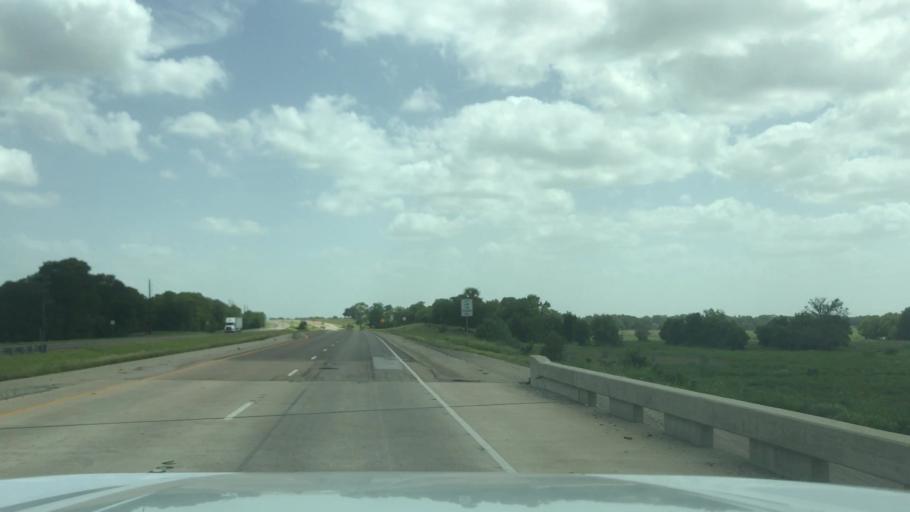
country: US
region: Texas
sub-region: Robertson County
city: Calvert
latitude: 31.0145
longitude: -96.7049
